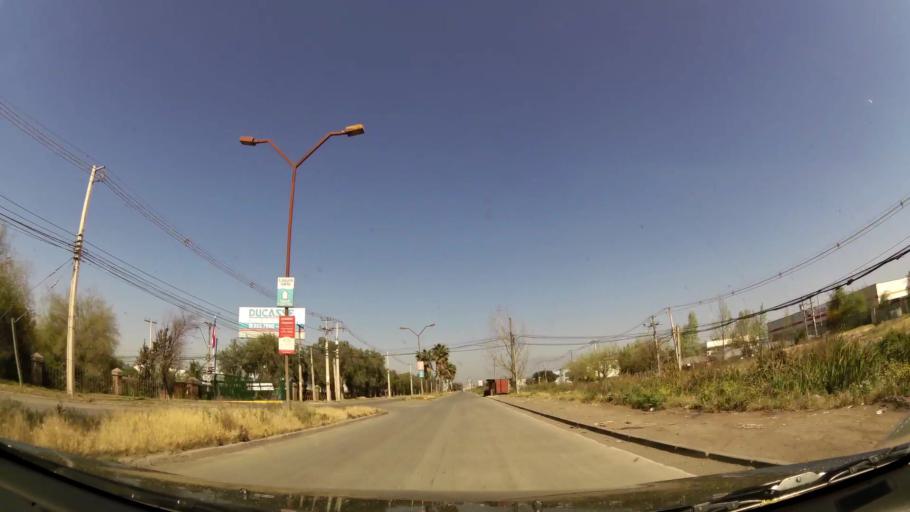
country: CL
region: Santiago Metropolitan
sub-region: Provincia de Chacabuco
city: Chicureo Abajo
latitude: -33.3164
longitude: -70.7298
